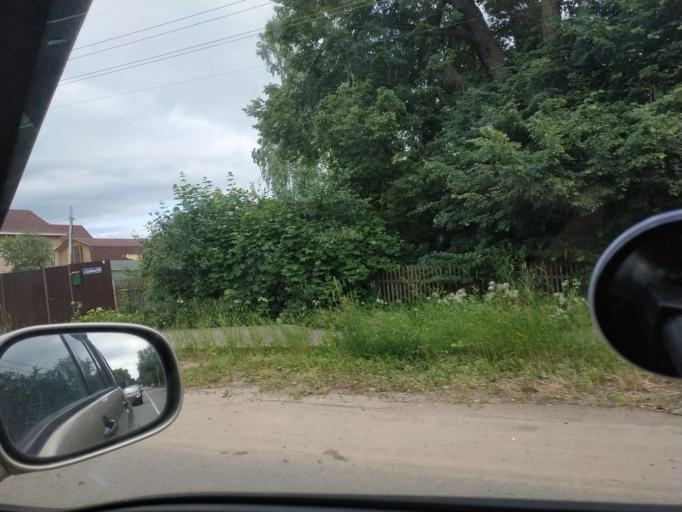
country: RU
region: Moskovskaya
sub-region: Shchelkovskiy Rayon
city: Grebnevo
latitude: 55.9894
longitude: 38.1266
